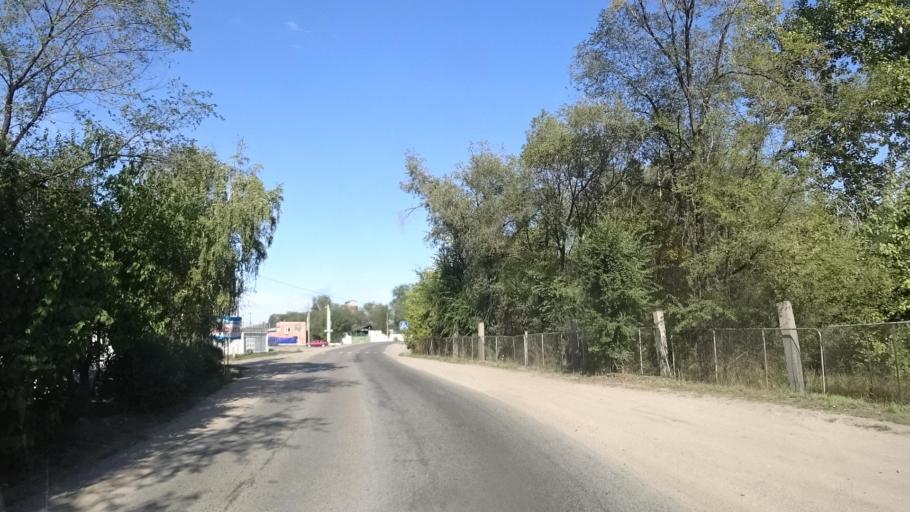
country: KZ
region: Almaty Oblysy
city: Energeticheskiy
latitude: 43.4197
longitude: 77.0074
